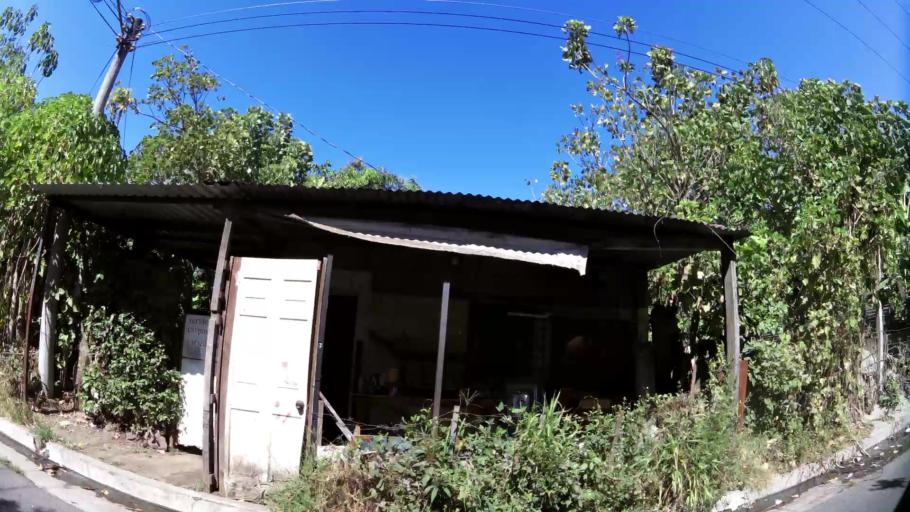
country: SV
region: La Libertad
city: Santa Tecla
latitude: 13.7332
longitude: -89.3773
